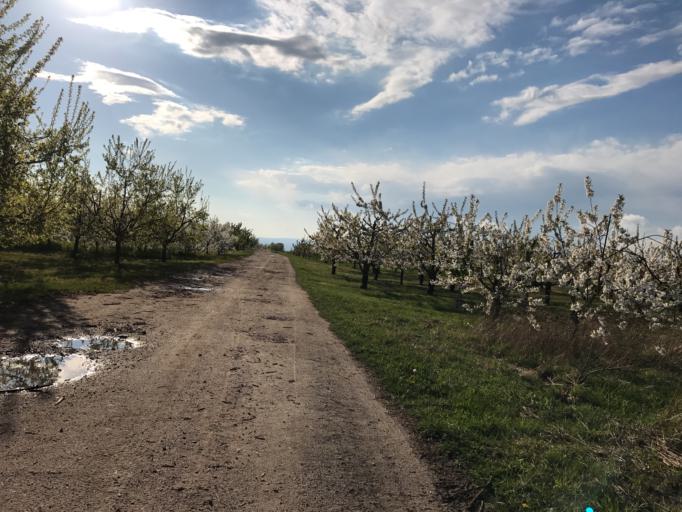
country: DE
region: Rheinland-Pfalz
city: Budenheim
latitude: 49.9888
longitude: 8.1507
